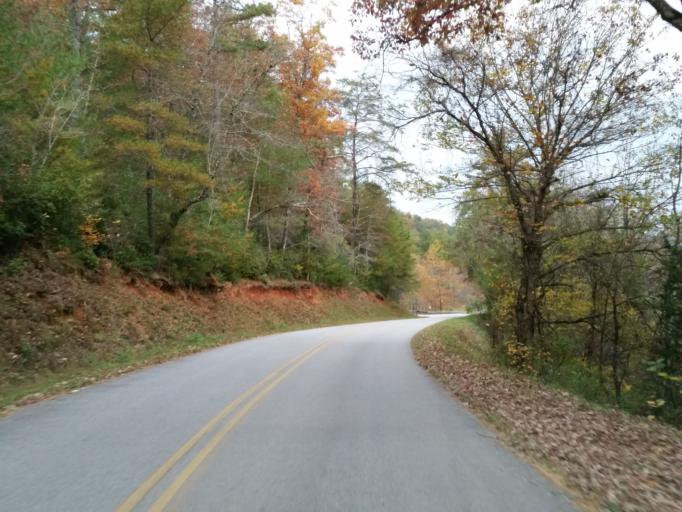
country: US
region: Georgia
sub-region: Fannin County
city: Blue Ridge
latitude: 34.7527
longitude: -84.1914
